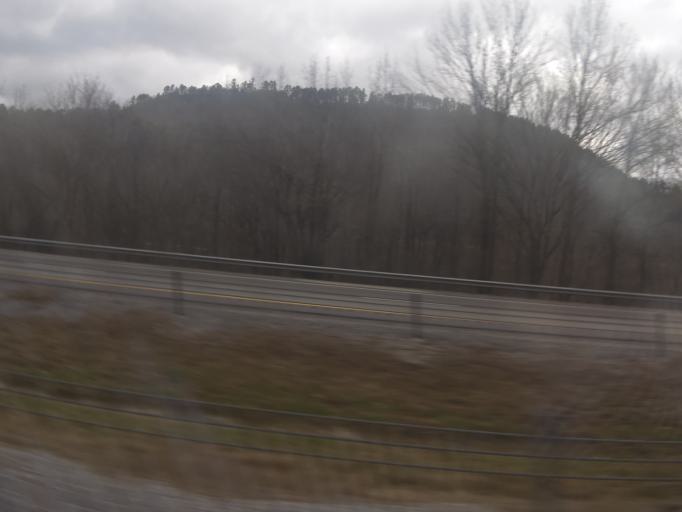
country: US
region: Georgia
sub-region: Dade County
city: Trenton
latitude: 34.9915
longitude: -85.4810
